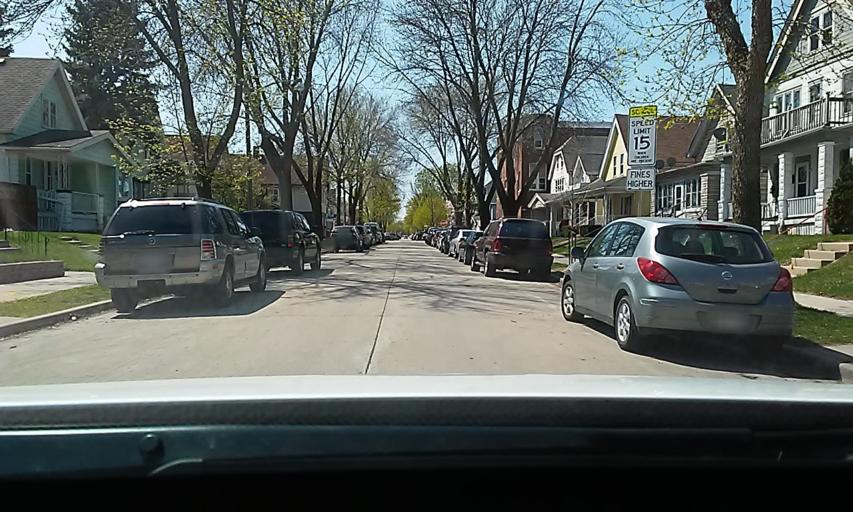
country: US
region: Wisconsin
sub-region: Milwaukee County
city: West Milwaukee
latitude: 43.0076
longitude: -87.9541
